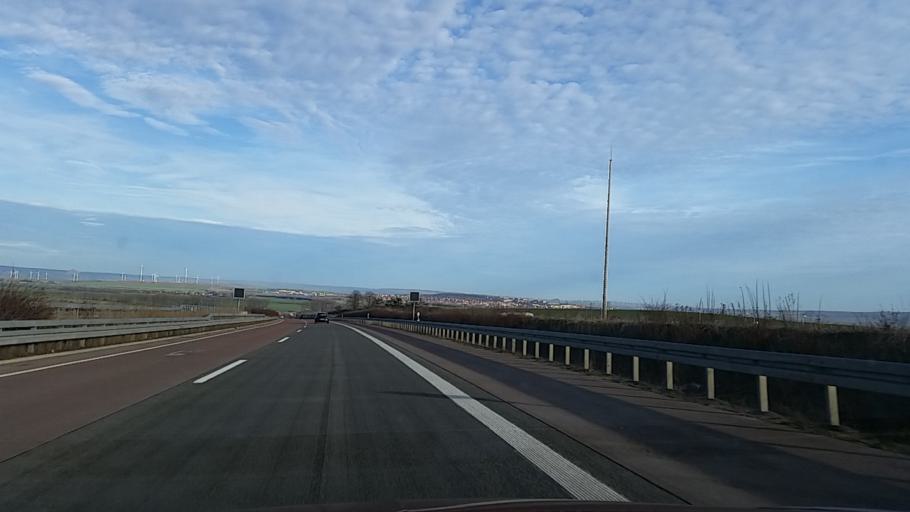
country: DE
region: Thuringia
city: Reinsdorf
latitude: 51.3306
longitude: 11.2519
